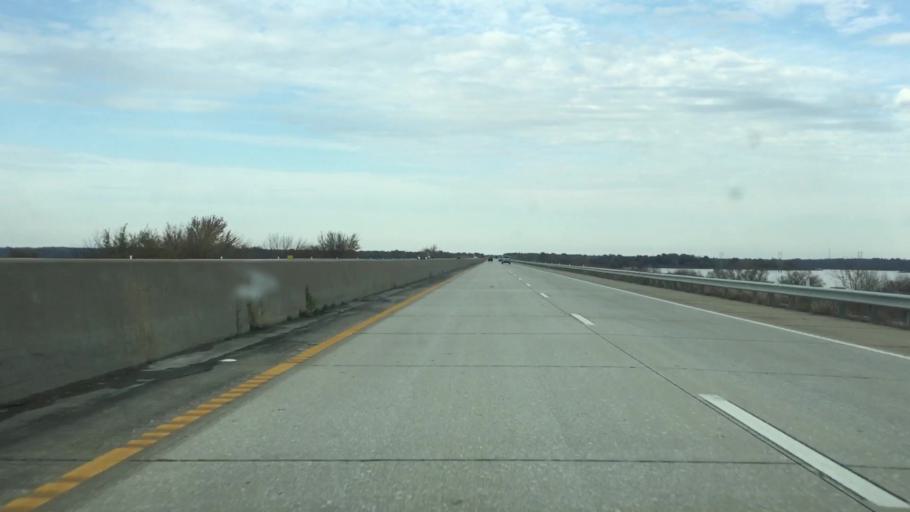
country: US
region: Missouri
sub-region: Henry County
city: Clinton
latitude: 38.3125
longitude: -93.7582
